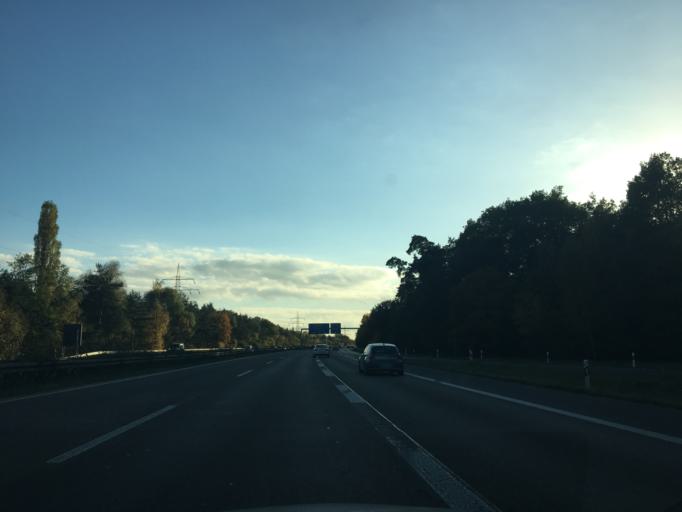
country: DE
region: Hesse
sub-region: Regierungsbezirk Darmstadt
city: Offenbach
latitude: 50.0775
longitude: 8.7357
